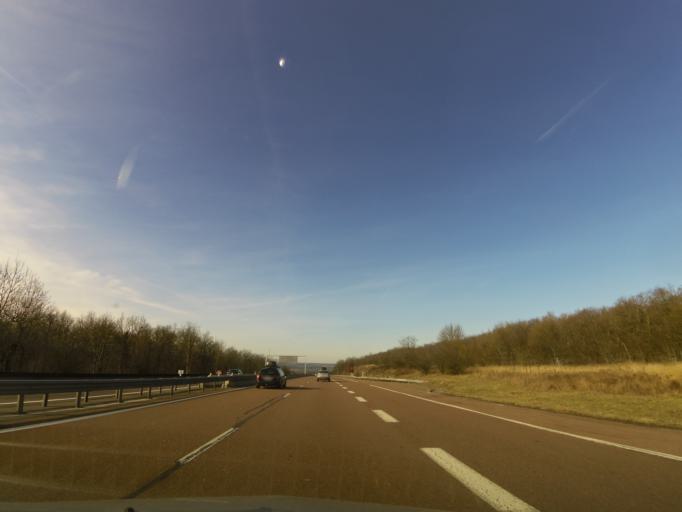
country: FR
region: Bourgogne
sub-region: Departement de la Cote-d'Or
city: Savigny-les-Beaune
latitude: 47.1178
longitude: 4.7066
